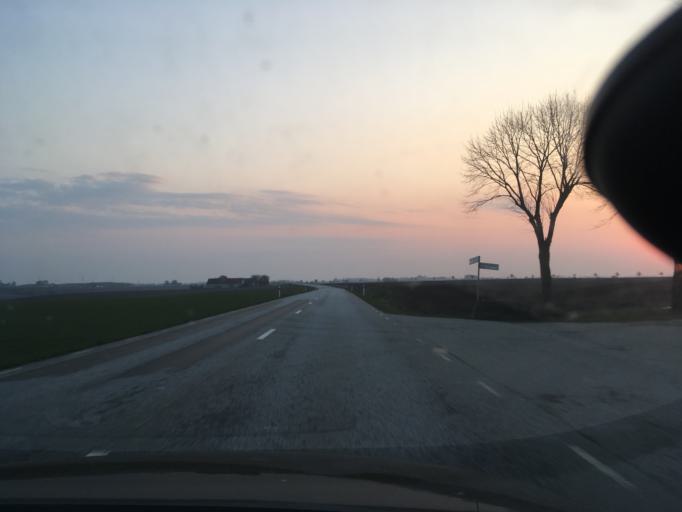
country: SE
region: Skane
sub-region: Ystads Kommun
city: Kopingebro
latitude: 55.4702
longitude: 14.0465
